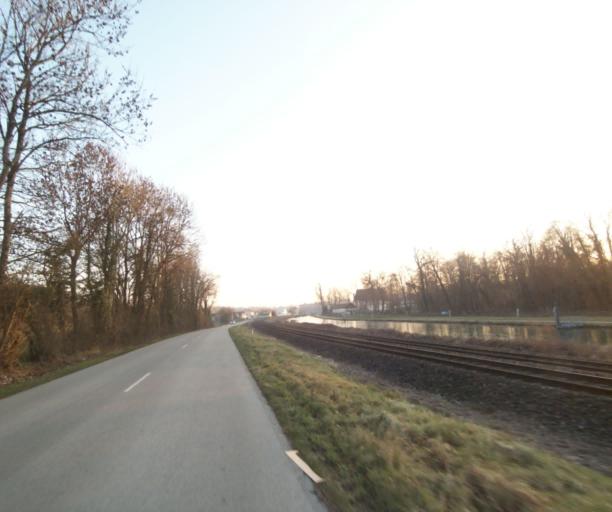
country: FR
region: Champagne-Ardenne
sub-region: Departement de la Haute-Marne
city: Bienville
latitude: 48.5865
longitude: 5.0445
